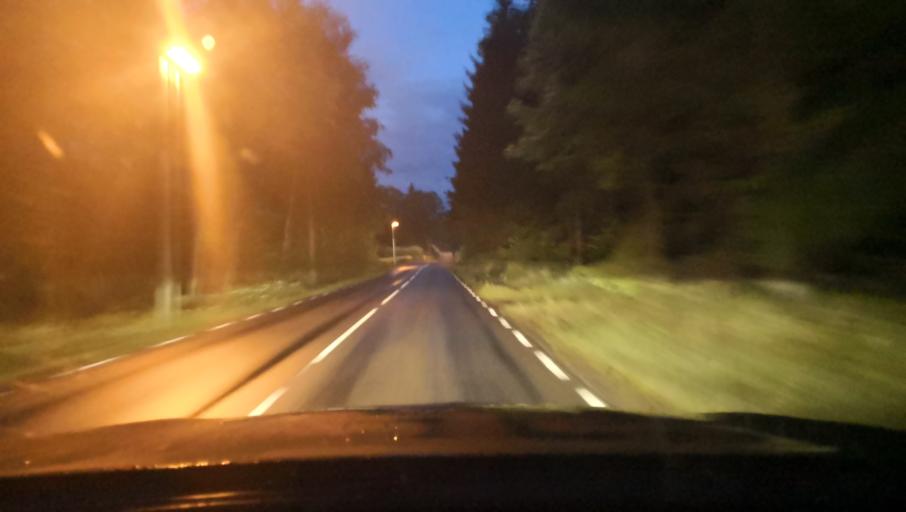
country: SE
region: Skane
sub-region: Hassleholms Kommun
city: Hastveda
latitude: 56.2964
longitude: 13.9464
